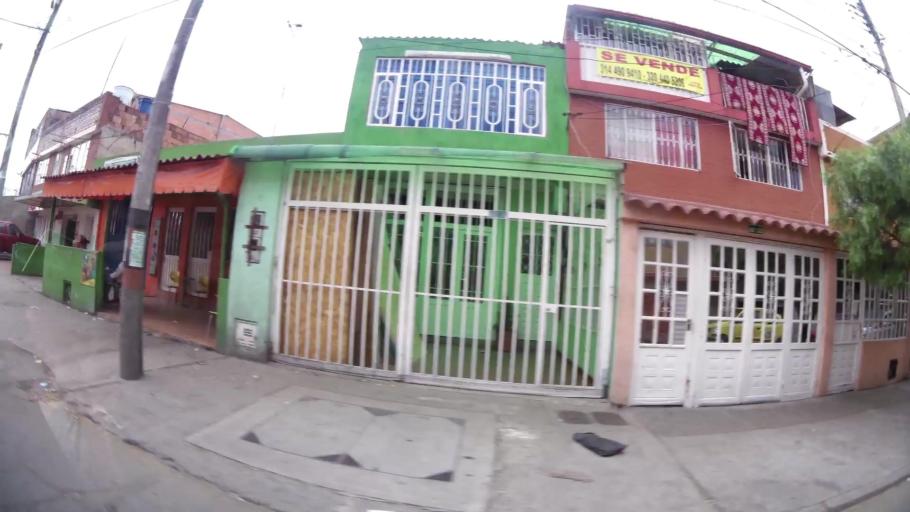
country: CO
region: Bogota D.C.
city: Bogota
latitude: 4.6007
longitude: -74.1421
